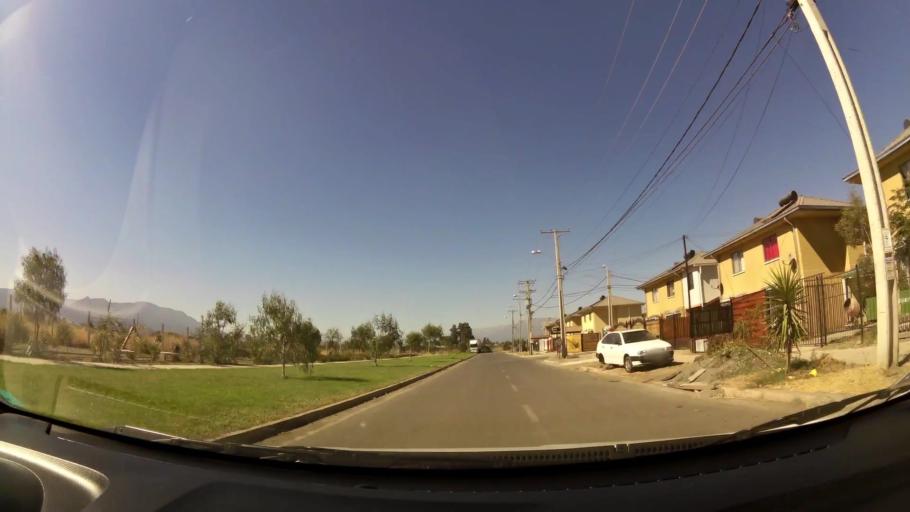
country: CL
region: O'Higgins
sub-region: Provincia de Cachapoal
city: Rancagua
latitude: -34.1745
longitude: -70.7754
